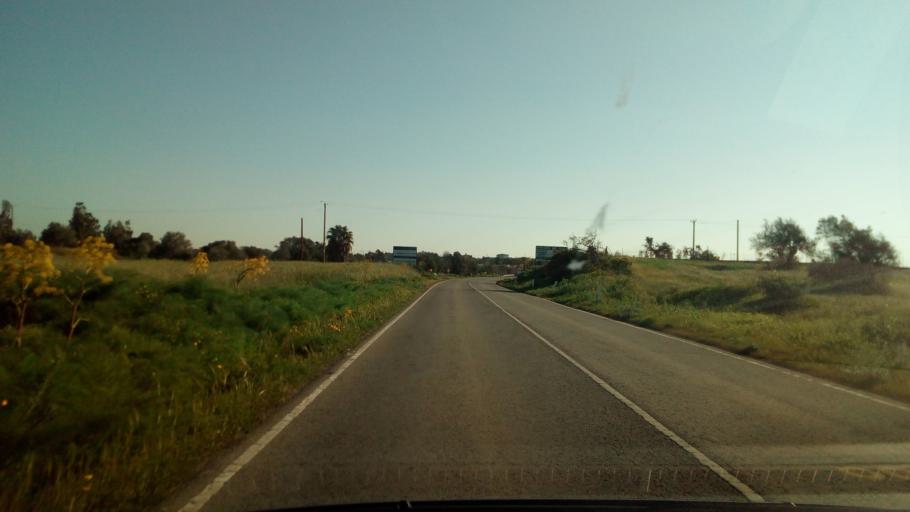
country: CY
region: Larnaka
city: Tersefanou
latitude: 34.7954
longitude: 33.4933
